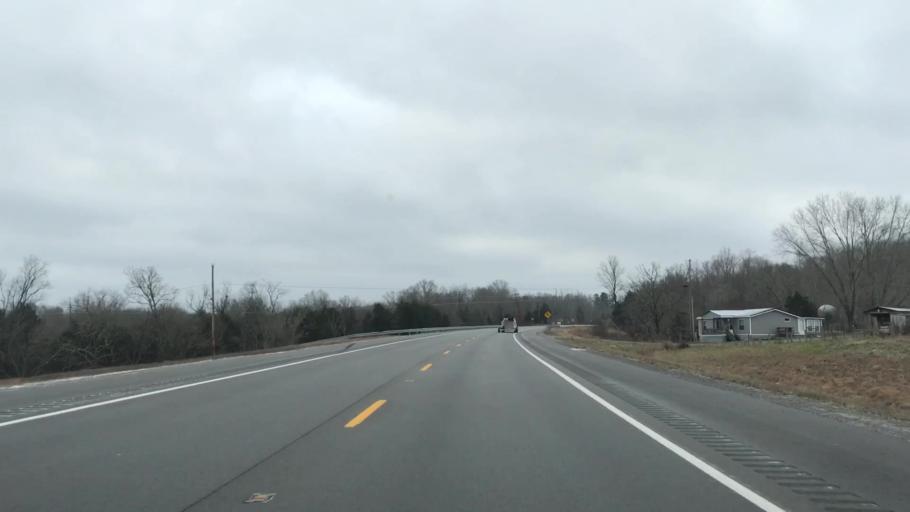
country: US
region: Kentucky
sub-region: Adair County
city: Columbia
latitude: 37.0529
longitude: -85.3613
